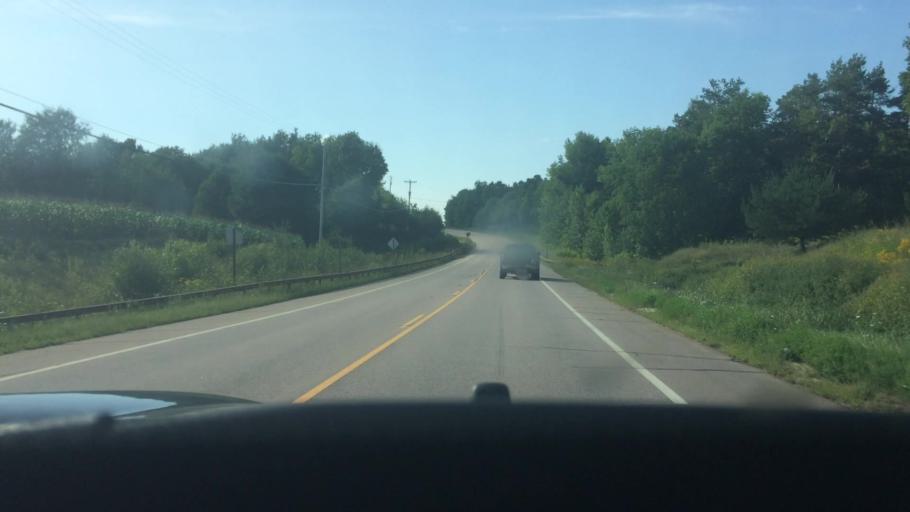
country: US
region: New York
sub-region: Franklin County
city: Malone
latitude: 44.8488
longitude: -74.1988
